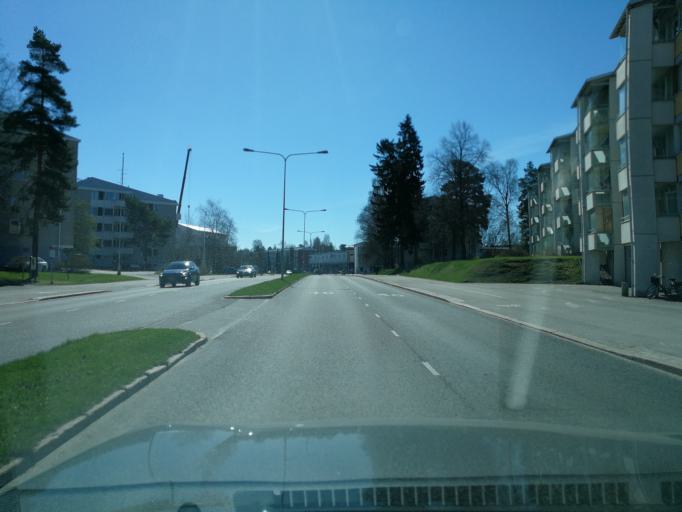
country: FI
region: Uusimaa
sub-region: Helsinki
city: Helsinki
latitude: 60.2334
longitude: 24.9320
